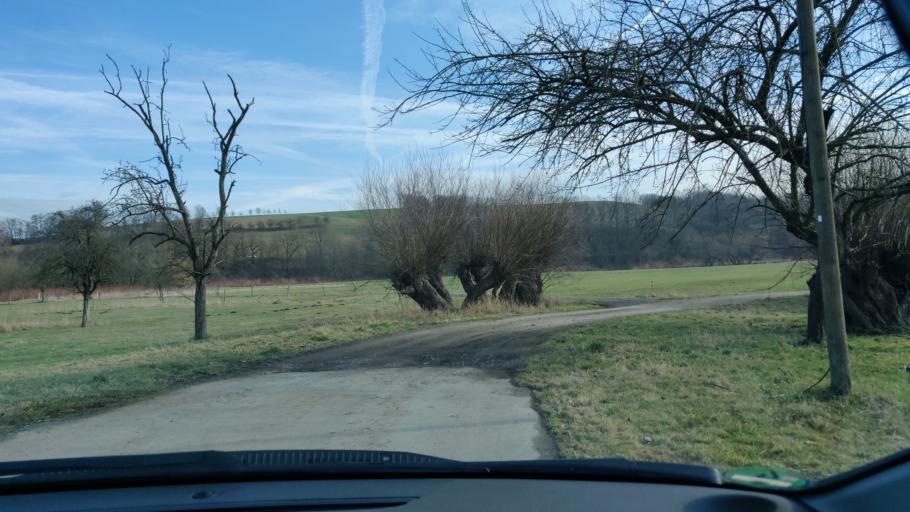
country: DE
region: Saxony
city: Rochlitz
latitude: 51.0804
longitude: 12.7981
